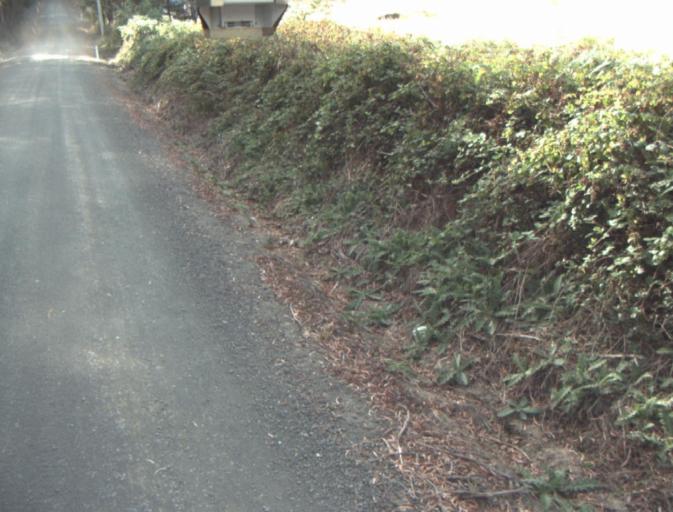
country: AU
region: Tasmania
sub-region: Launceston
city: Mayfield
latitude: -41.2704
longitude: 147.1686
